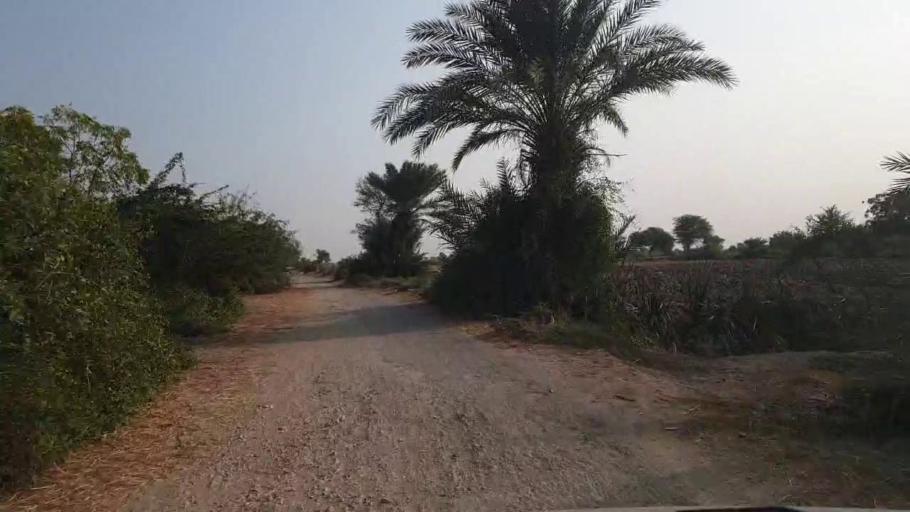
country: PK
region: Sindh
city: Matli
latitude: 25.0622
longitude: 68.7605
